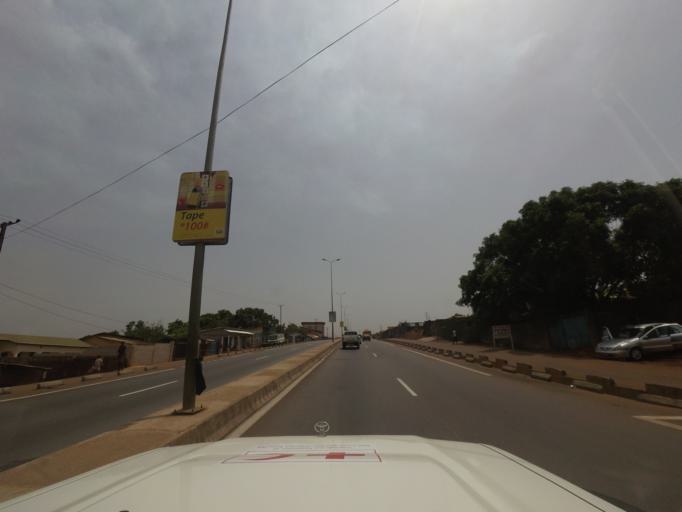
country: GN
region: Kindia
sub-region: Prefecture de Dubreka
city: Dubreka
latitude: 9.6923
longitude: -13.5082
